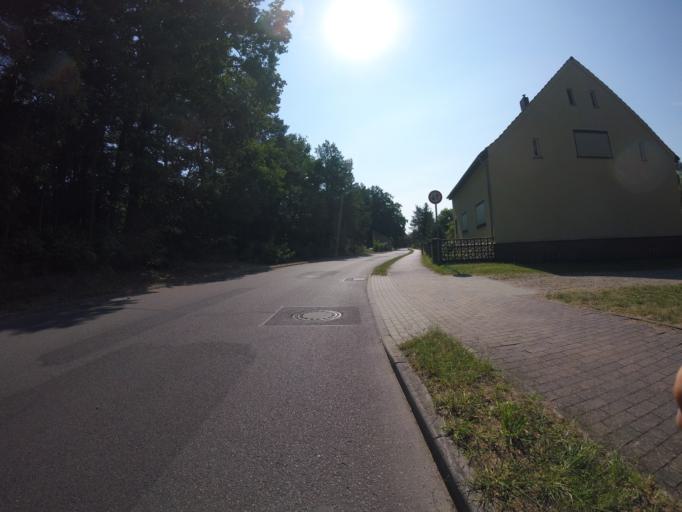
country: DE
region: Brandenburg
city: Mullrose
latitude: 52.2687
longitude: 14.3569
